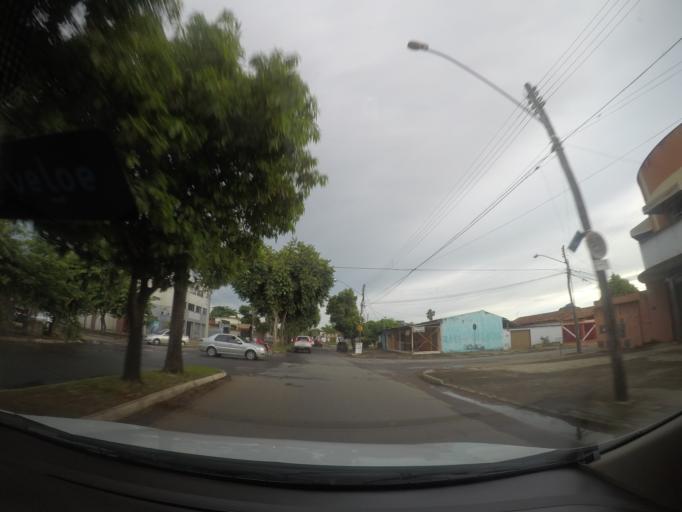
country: BR
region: Goias
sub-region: Goiania
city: Goiania
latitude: -16.7157
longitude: -49.3106
